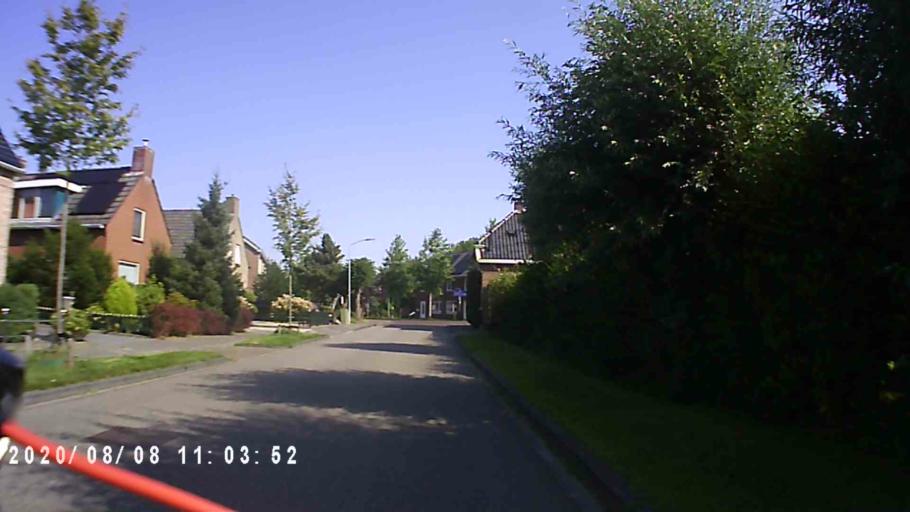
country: NL
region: Groningen
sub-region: Gemeente Leek
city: Leek
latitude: 53.1602
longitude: 6.3944
